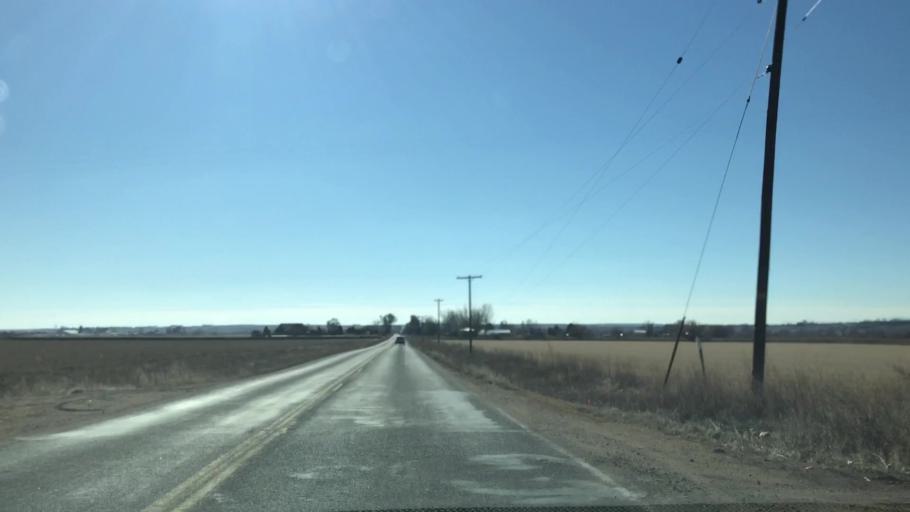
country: US
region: Colorado
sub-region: Weld County
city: Windsor
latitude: 40.5048
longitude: -104.9442
